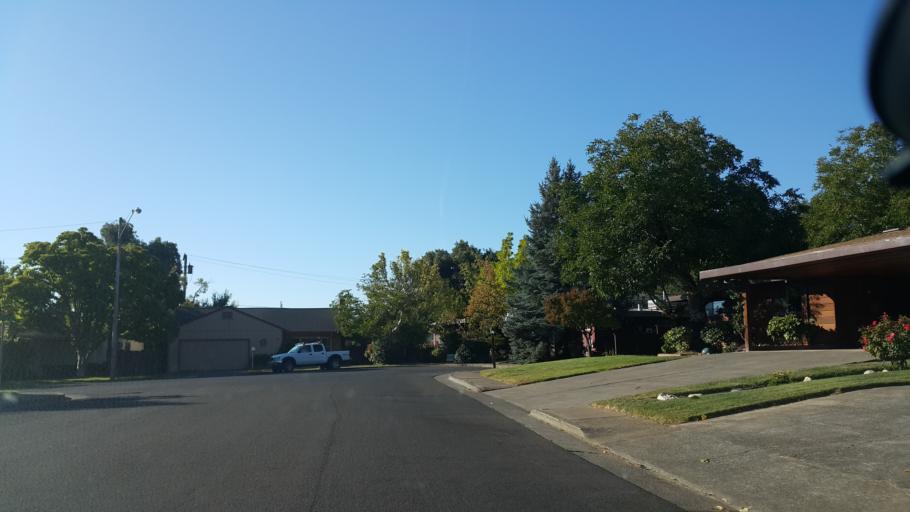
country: US
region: California
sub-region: Mendocino County
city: Ukiah
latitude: 39.1427
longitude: -123.2127
